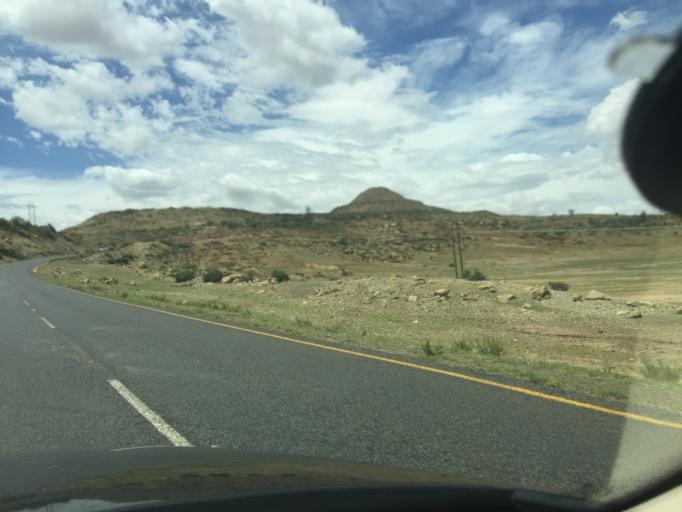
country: LS
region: Mohale's Hoek District
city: Mohale's Hoek
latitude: -30.0596
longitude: 27.4134
